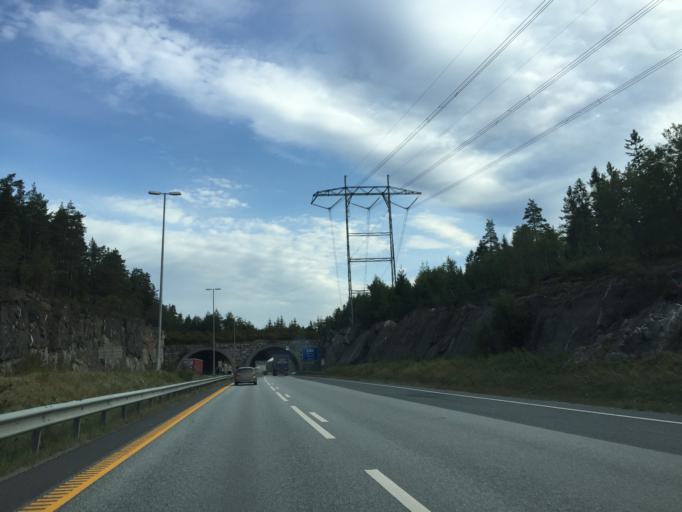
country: NO
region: Akershus
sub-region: Oppegard
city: Kolbotn
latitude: 59.7871
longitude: 10.8392
